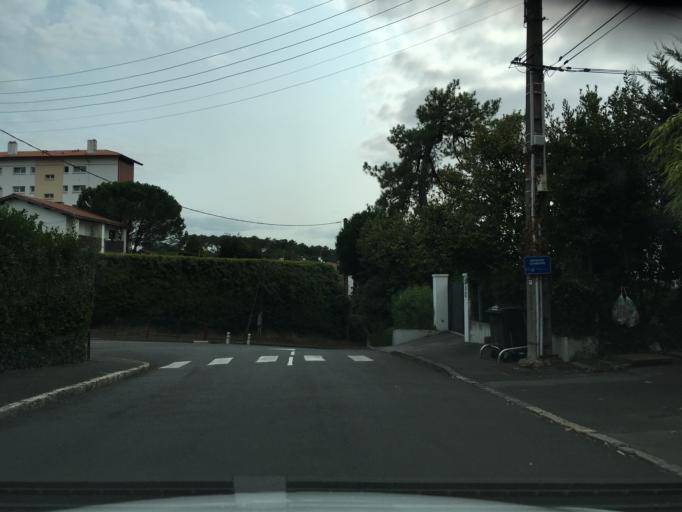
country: FR
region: Aquitaine
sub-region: Departement des Pyrenees-Atlantiques
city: Biarritz
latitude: 43.4749
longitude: -1.5431
